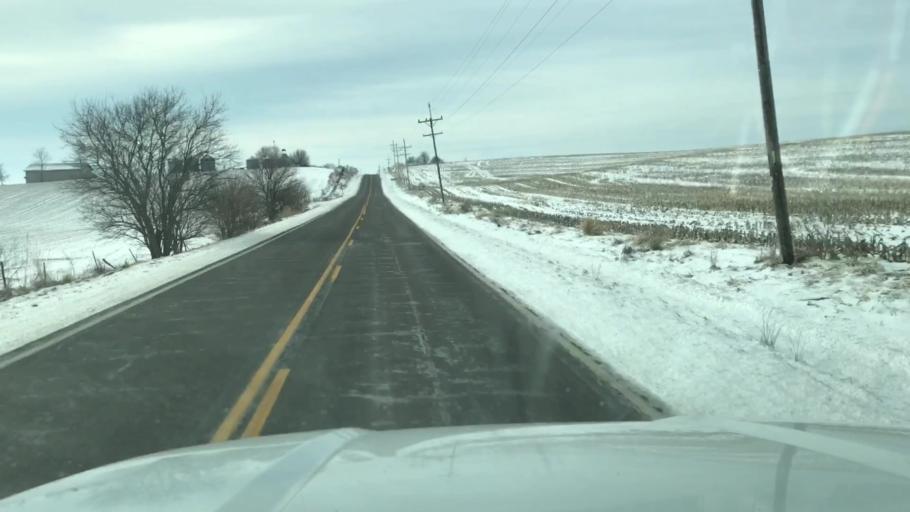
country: US
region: Missouri
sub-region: Holt County
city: Oregon
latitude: 40.0681
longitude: -95.1356
